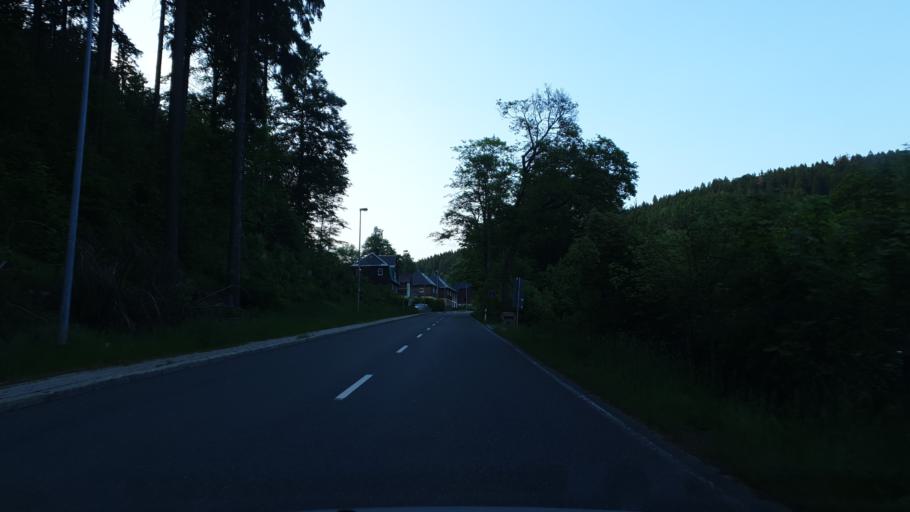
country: DE
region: Saxony
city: Klingenthal
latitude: 50.3888
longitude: 12.4927
